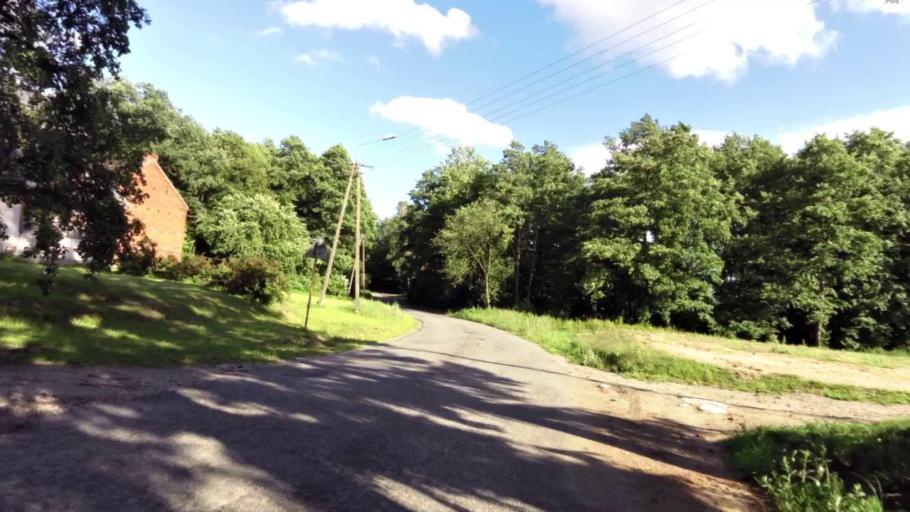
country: PL
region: West Pomeranian Voivodeship
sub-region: Powiat slawienski
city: Slawno
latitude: 54.4355
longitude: 16.7661
